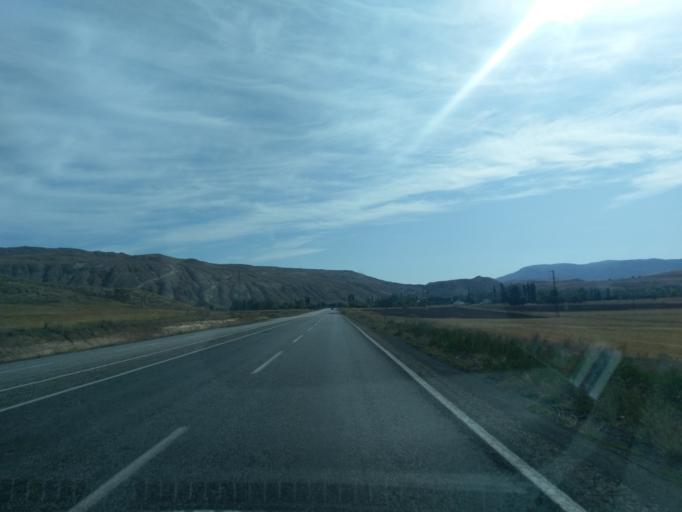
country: TR
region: Sivas
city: Zara
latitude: 39.8619
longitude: 37.8128
